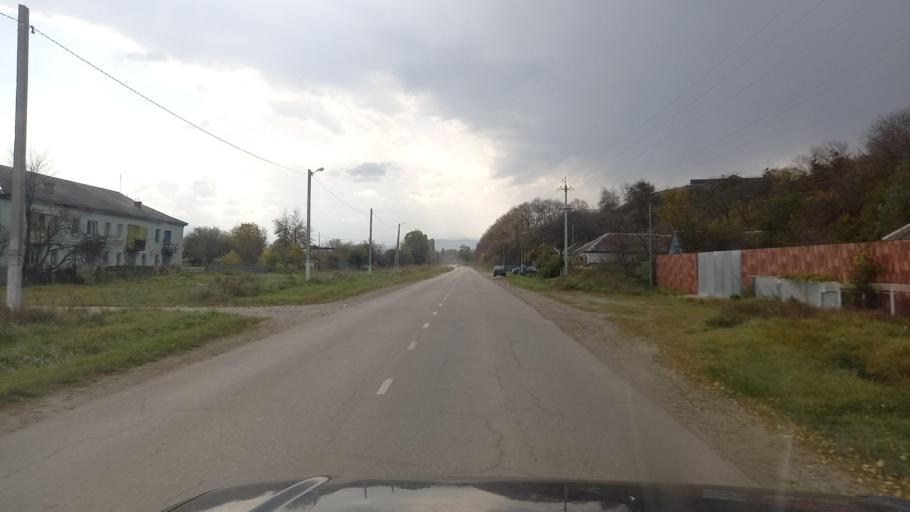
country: RU
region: Krasnodarskiy
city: Psebay
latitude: 44.1377
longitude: 40.8182
